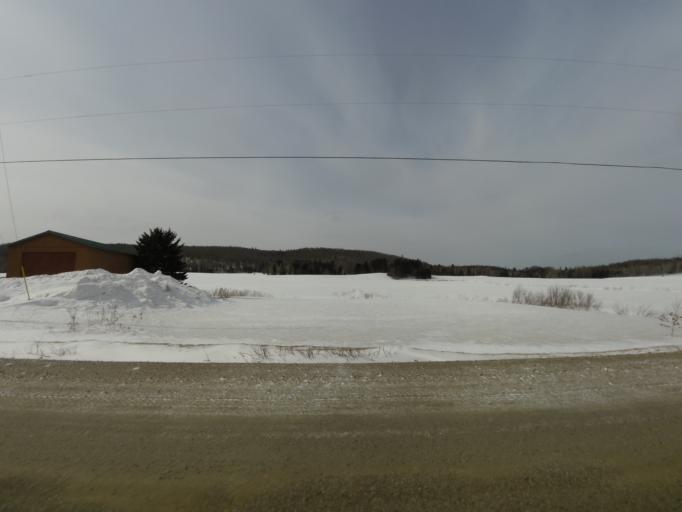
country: CA
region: Quebec
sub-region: Laurentides
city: Ferme-Neuve
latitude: 46.9333
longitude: -75.3545
